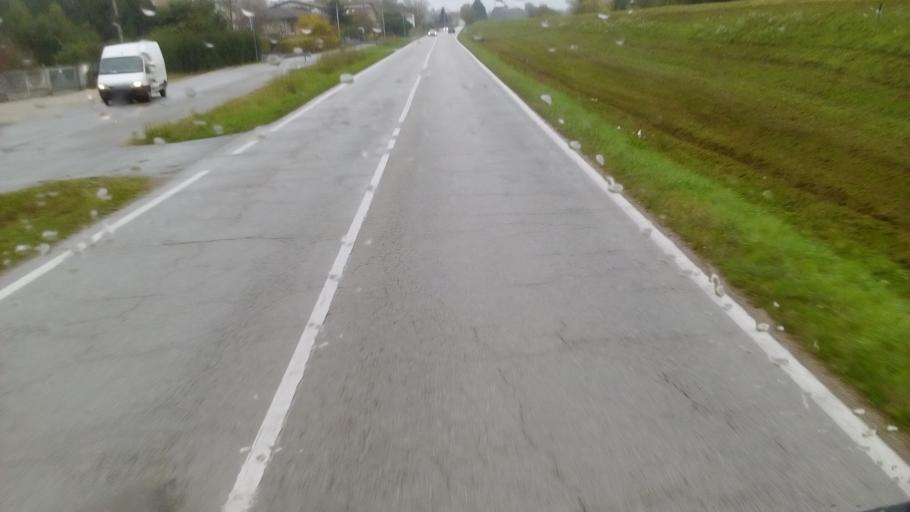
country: IT
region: Veneto
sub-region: Provincia di Vicenza
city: Montecchio Precalcino
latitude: 45.6546
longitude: 11.5739
